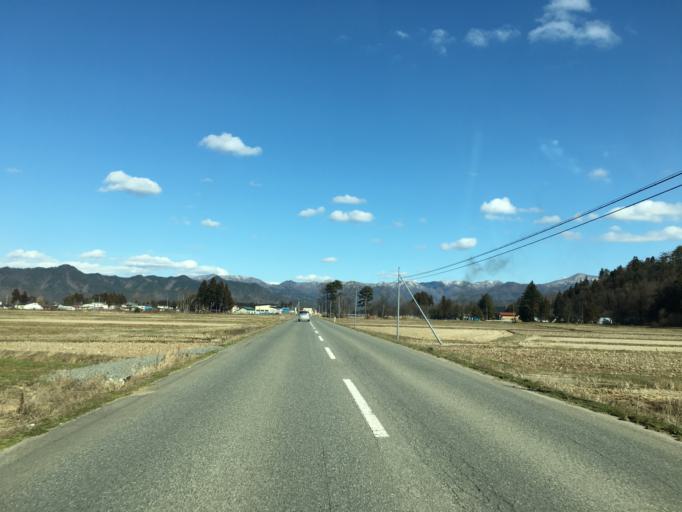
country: JP
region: Yamagata
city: Yonezawa
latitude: 37.9519
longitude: 140.1484
